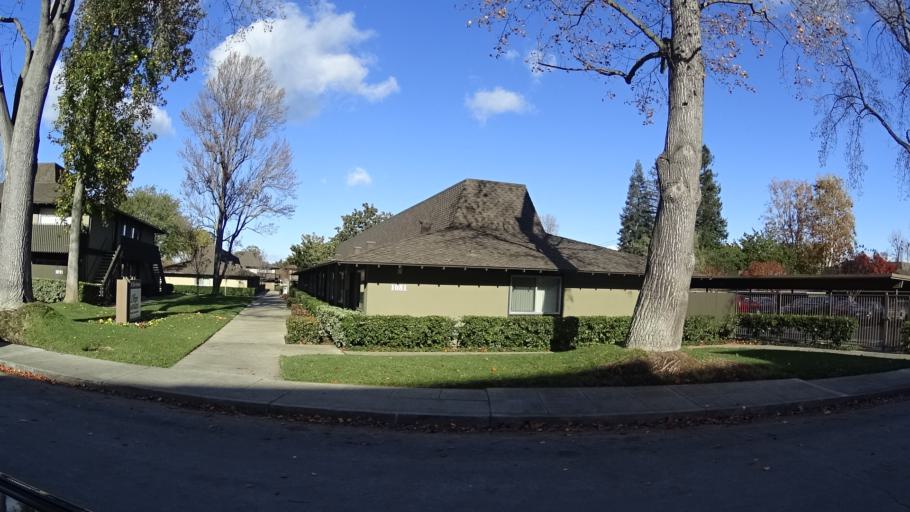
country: US
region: California
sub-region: Santa Clara County
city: Sunnyvale
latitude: 37.3738
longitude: -122.0510
